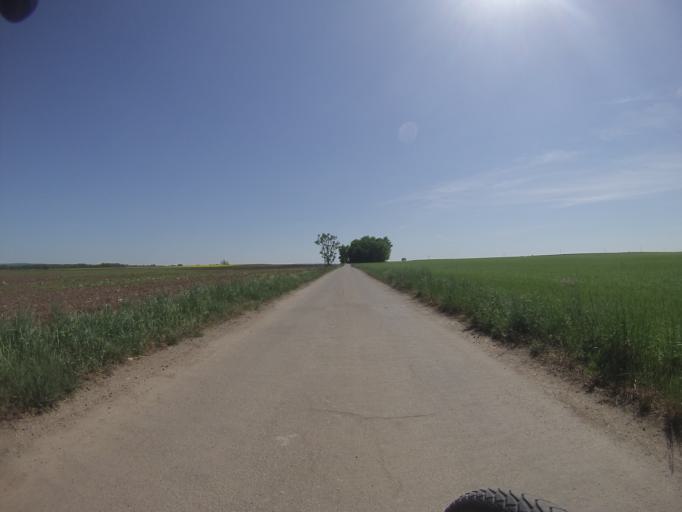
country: CZ
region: South Moravian
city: Hrusovany nad Jevisovkou
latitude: 48.8072
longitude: 16.4243
